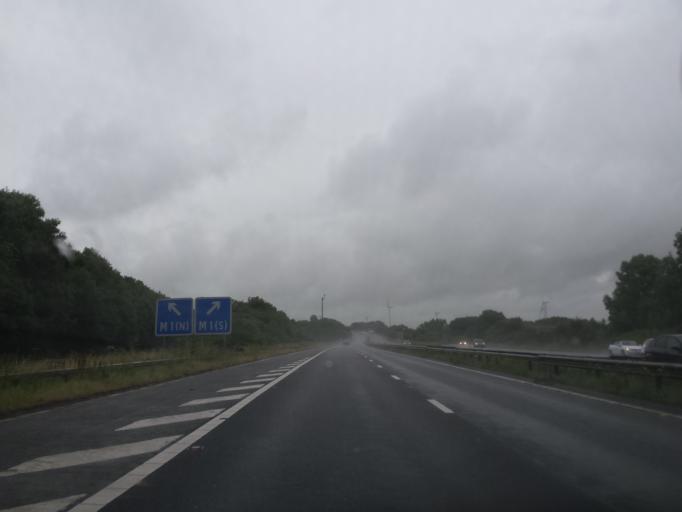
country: GB
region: England
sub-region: Rotherham
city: Bramley
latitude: 53.3995
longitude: -1.2660
